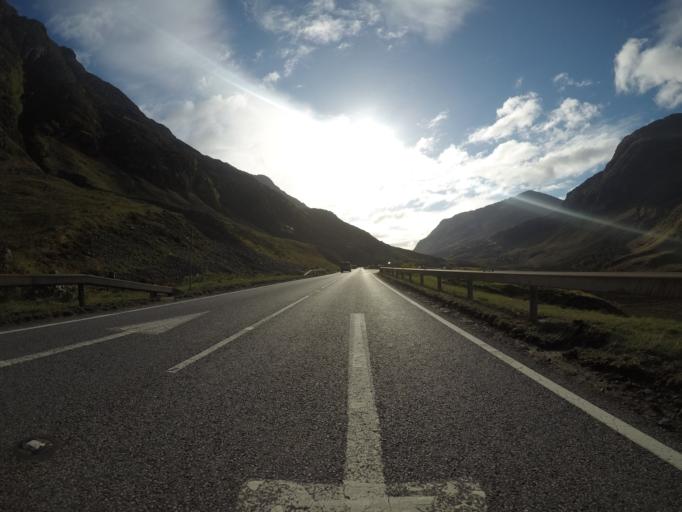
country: GB
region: Scotland
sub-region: Highland
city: Fort William
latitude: 56.6682
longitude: -4.9918
